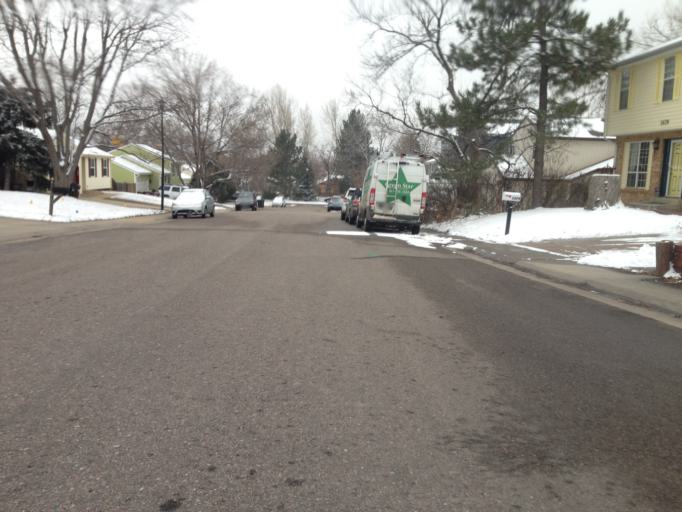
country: US
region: Colorado
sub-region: Boulder County
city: Louisville
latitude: 39.9846
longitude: -105.1400
